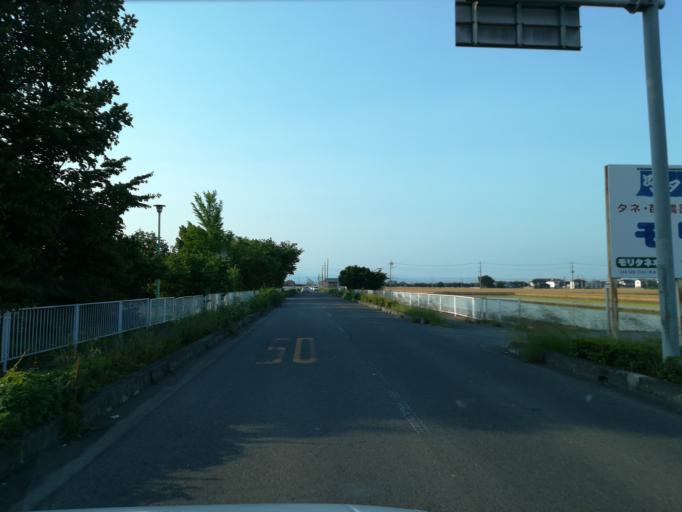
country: JP
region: Saitama
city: Menuma
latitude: 36.1898
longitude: 139.3777
